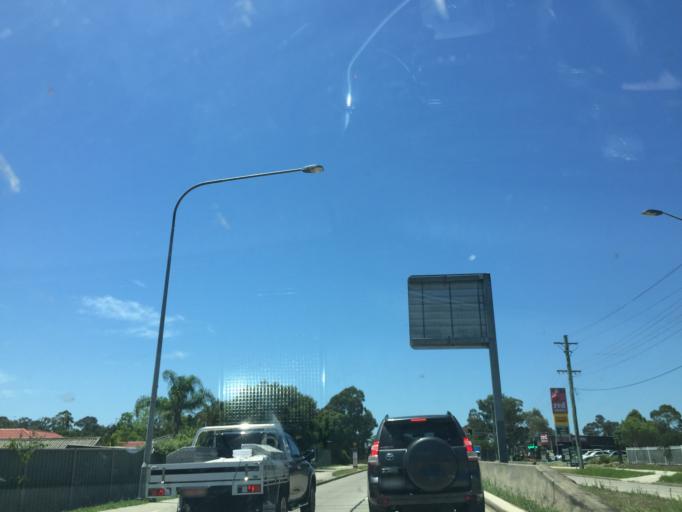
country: AU
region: New South Wales
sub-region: Blacktown
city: Glendenning
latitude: -33.7348
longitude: 150.8508
